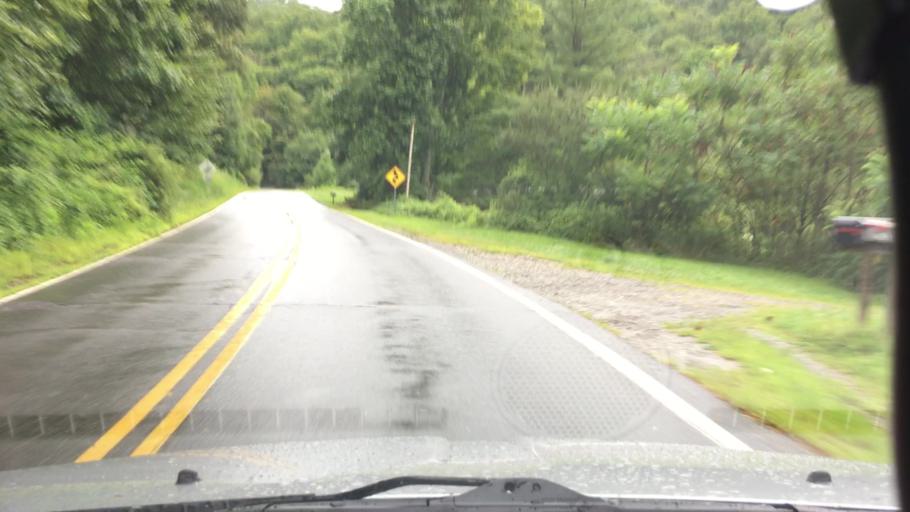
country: US
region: North Carolina
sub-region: Madison County
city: Mars Hill
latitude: 35.9181
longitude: -82.5355
